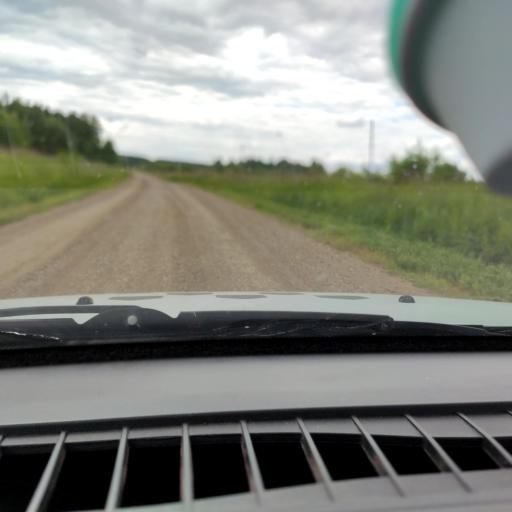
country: RU
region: Perm
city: Suksun
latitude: 57.2037
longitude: 57.6193
